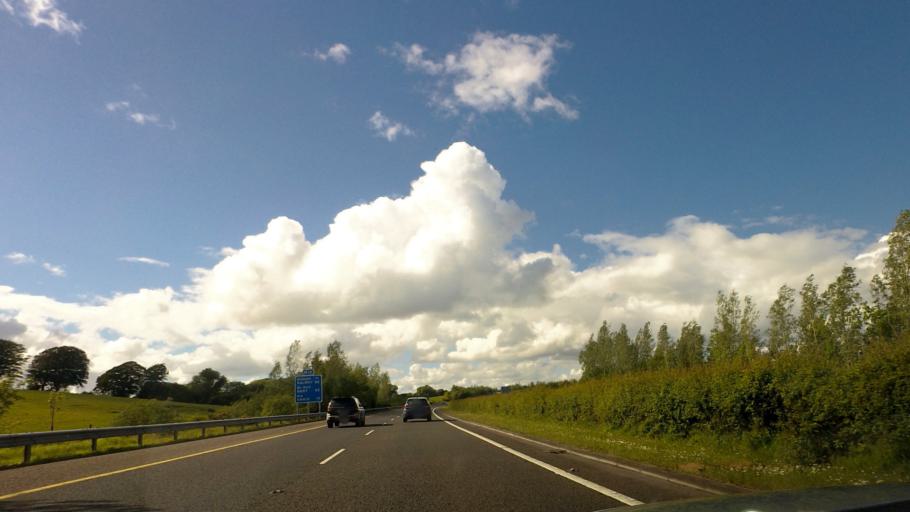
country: IE
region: Munster
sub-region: An Clar
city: Newmarket on Fergus
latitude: 52.7321
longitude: -8.8867
